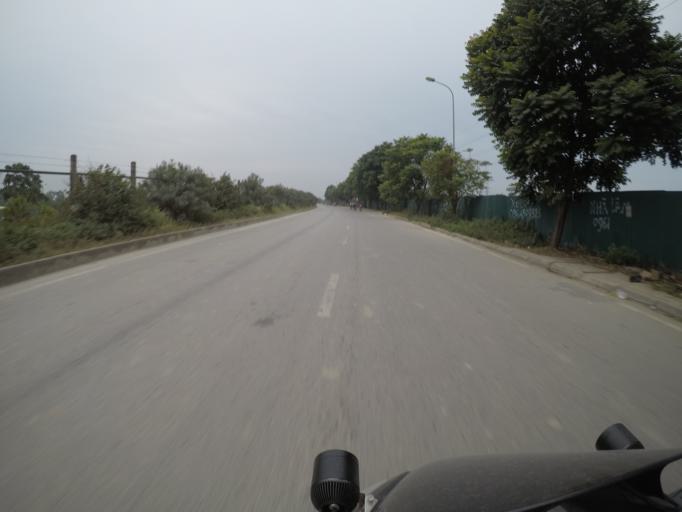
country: VN
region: Ha Noi
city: Cau Dien
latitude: 21.0067
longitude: 105.7652
